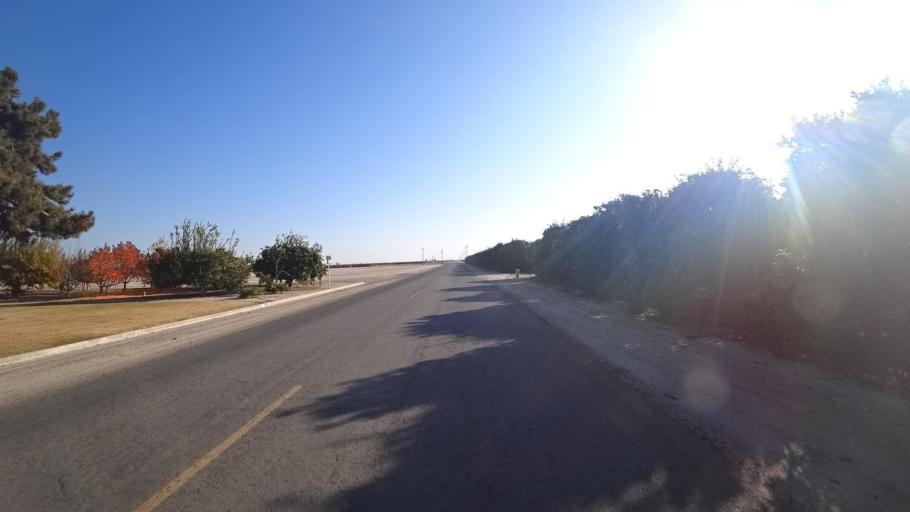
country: US
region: California
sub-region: Kern County
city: Delano
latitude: 35.7686
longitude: -119.1903
